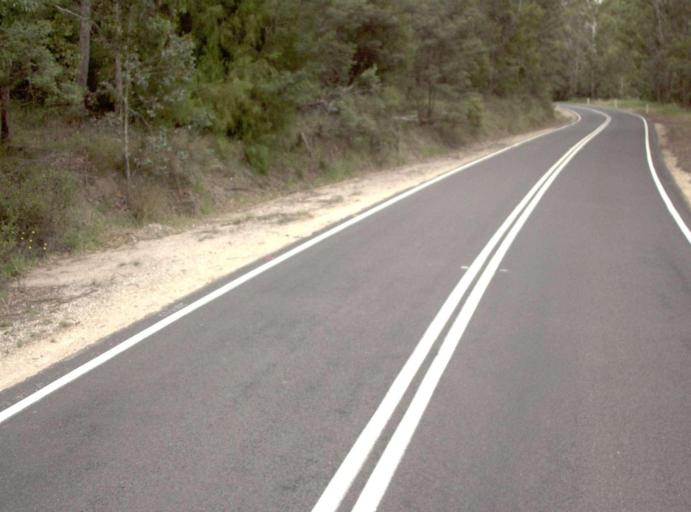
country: AU
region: New South Wales
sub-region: Bombala
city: Bombala
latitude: -37.4589
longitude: 149.1885
